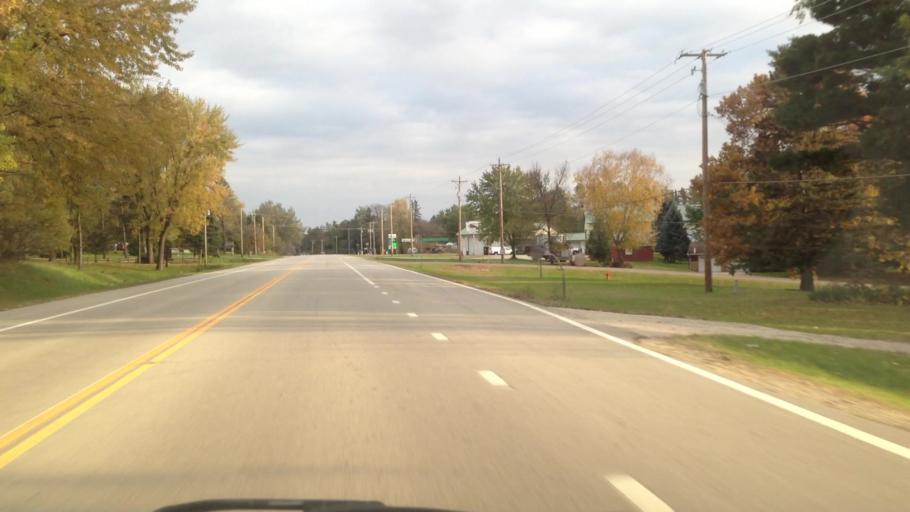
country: US
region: Minnesota
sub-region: Olmsted County
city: Rochester
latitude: 43.9764
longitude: -92.3950
